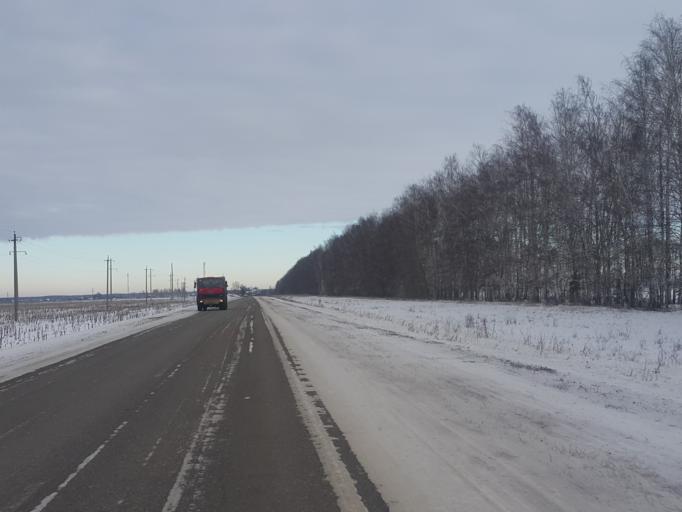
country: RU
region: Tambov
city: Rasskazovo
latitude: 52.8154
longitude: 41.7945
